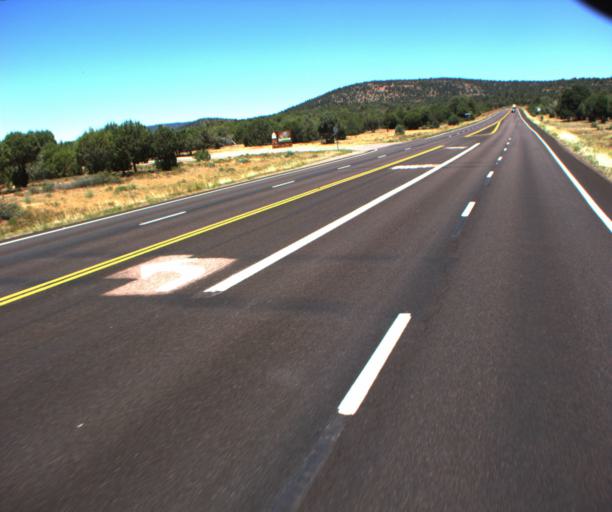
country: US
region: Arizona
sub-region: Gila County
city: Pine
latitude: 34.3345
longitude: -111.4204
